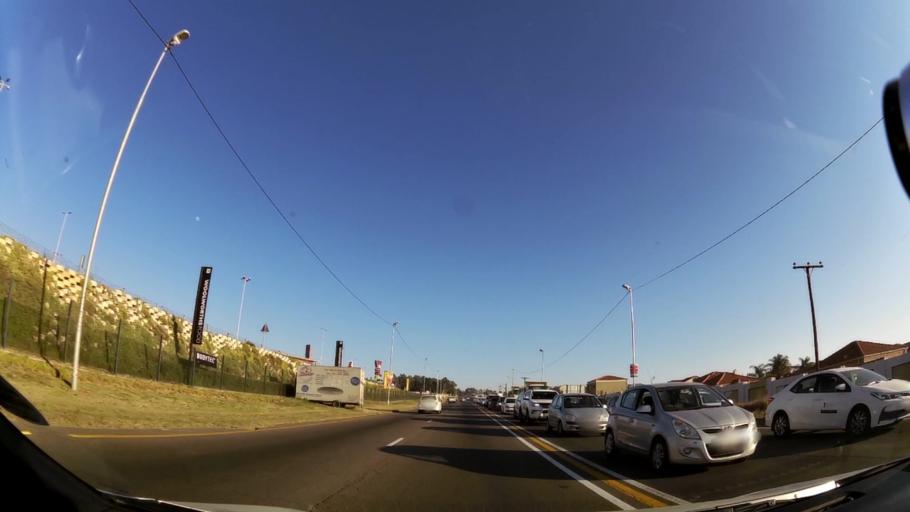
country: ZA
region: Gauteng
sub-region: City of Johannesburg Metropolitan Municipality
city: Midrand
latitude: -25.9446
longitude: 28.1080
